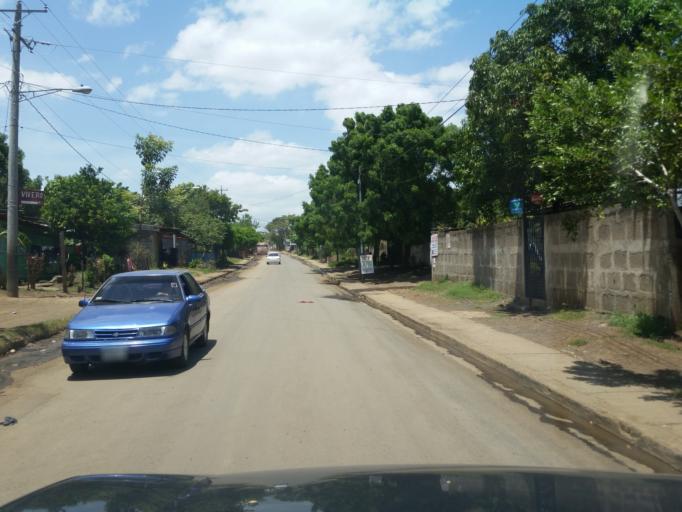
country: NI
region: Managua
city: Managua
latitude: 12.1182
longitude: -86.2166
